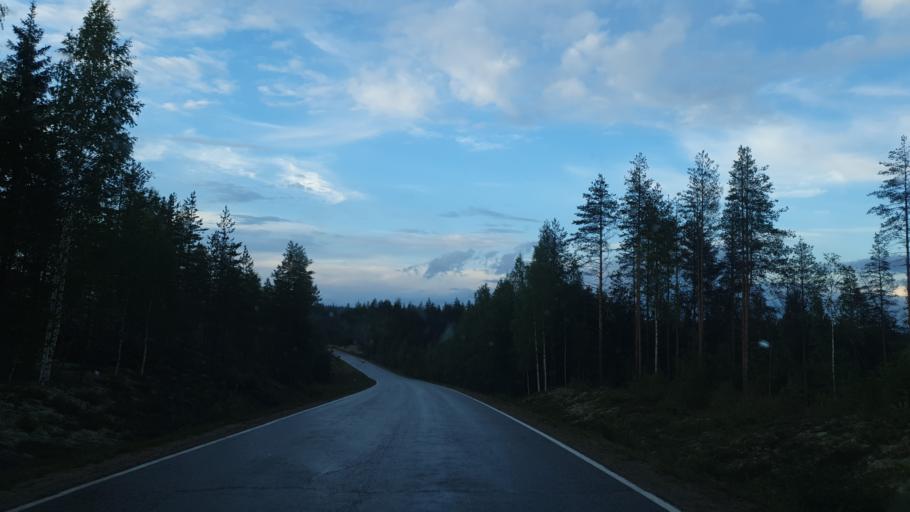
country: FI
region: North Karelia
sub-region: Pielisen Karjala
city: Lieksa
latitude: 63.7555
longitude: 29.8620
